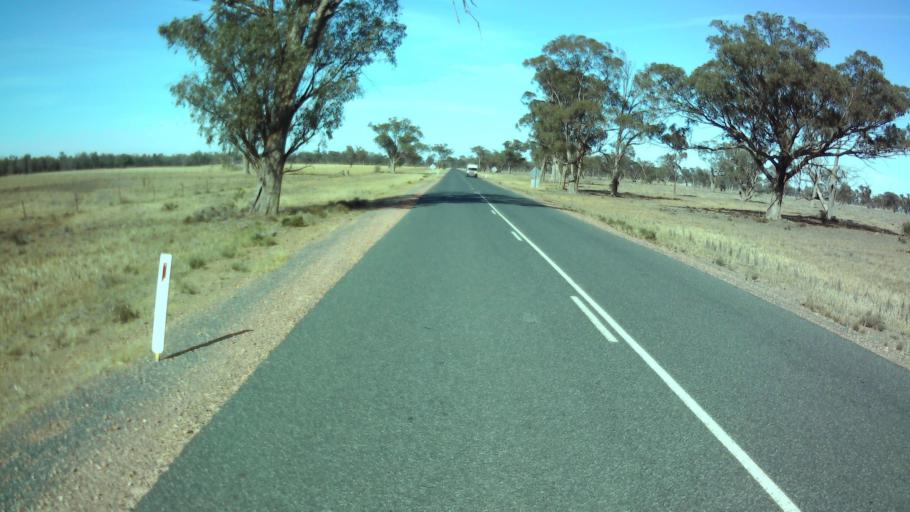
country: AU
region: New South Wales
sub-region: Weddin
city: Grenfell
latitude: -34.1072
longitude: 147.8606
